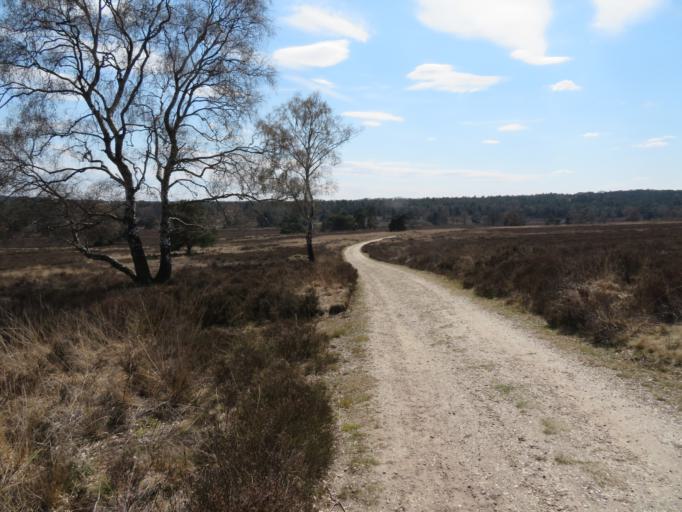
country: NL
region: Gelderland
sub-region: Gemeente Apeldoorn
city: Loenen
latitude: 52.0830
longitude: 6.0057
